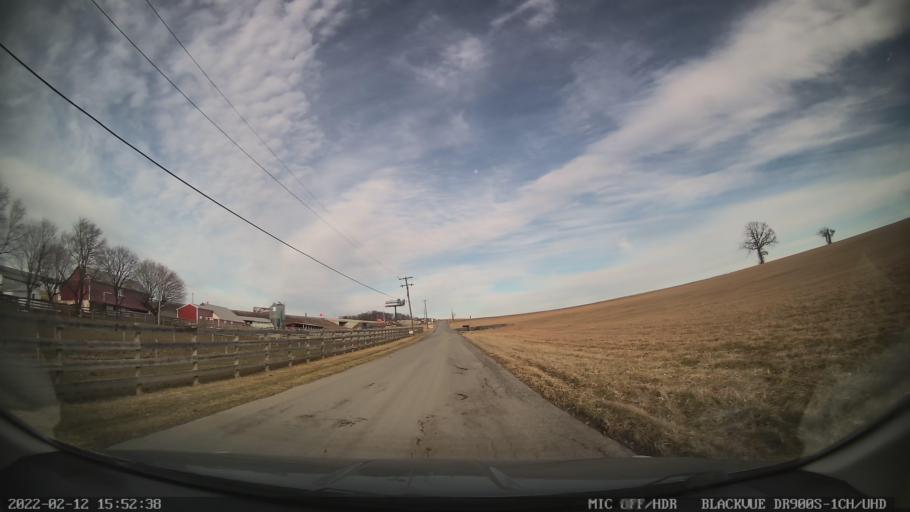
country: US
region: Pennsylvania
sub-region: Berks County
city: Kutztown
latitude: 40.5745
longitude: -75.7676
